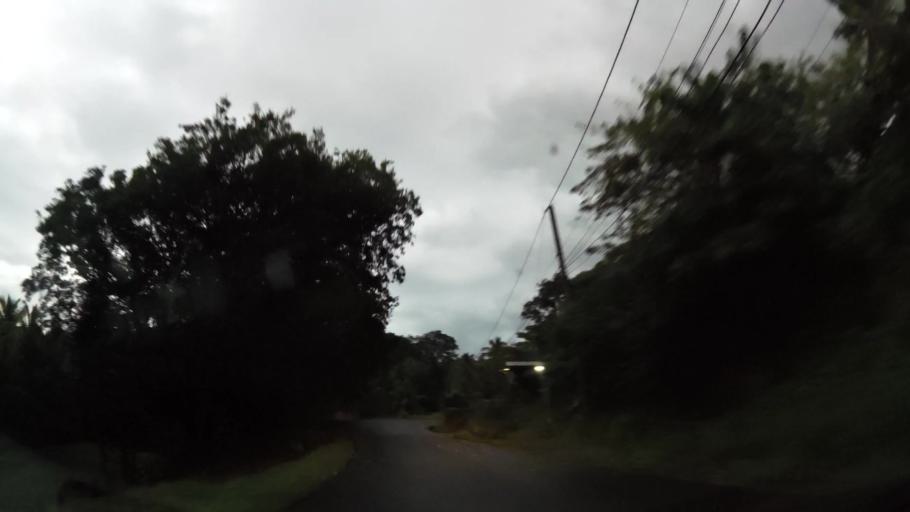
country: DM
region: Saint Andrew
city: Woodford Hill
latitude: 15.5864
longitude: -61.3278
